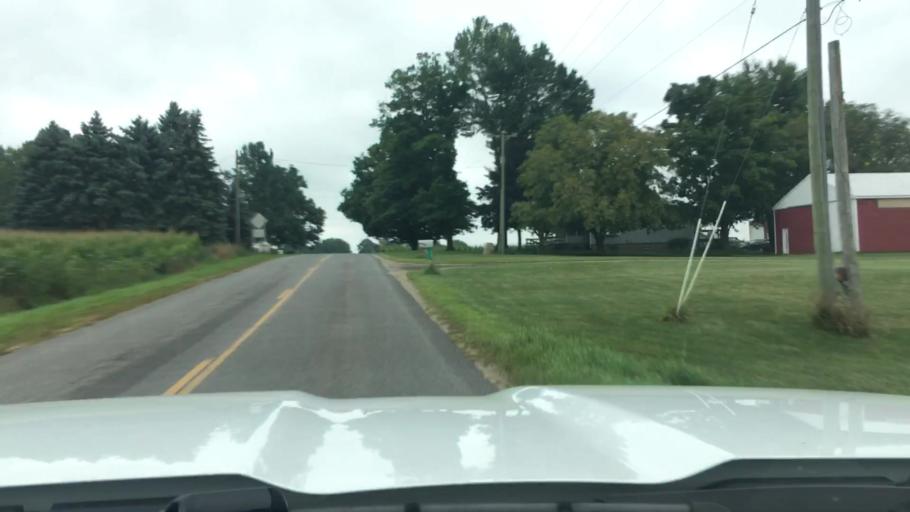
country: US
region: Michigan
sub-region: Ottawa County
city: Hudsonville
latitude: 42.7941
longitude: -85.8617
